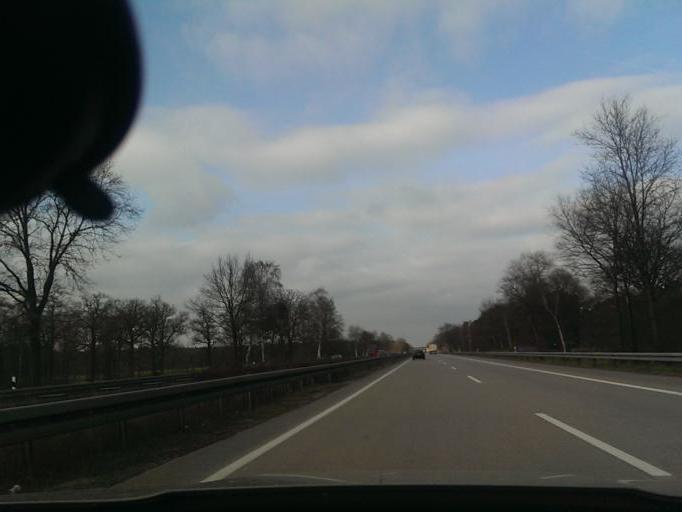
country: DE
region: Lower Saxony
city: Elze
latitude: 52.5222
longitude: 9.7805
